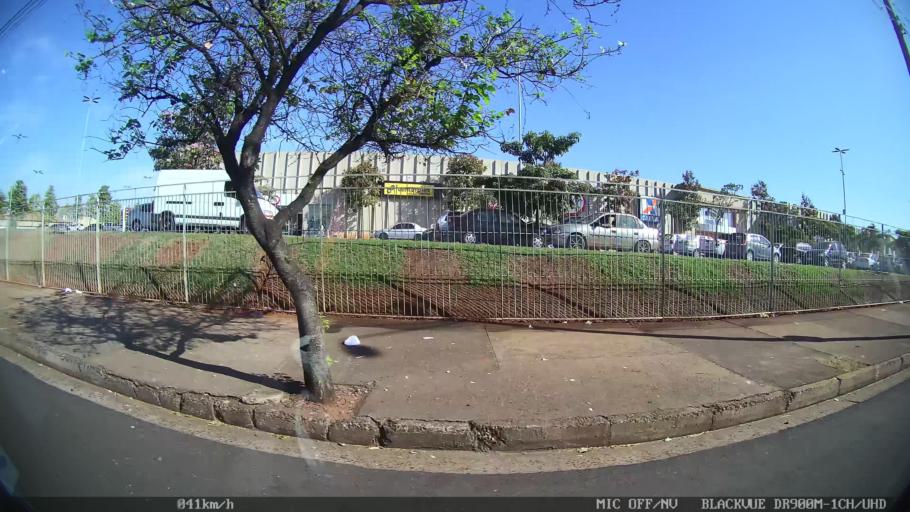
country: BR
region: Sao Paulo
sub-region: Sao Jose Do Rio Preto
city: Sao Jose do Rio Preto
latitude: -20.7705
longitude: -49.3851
